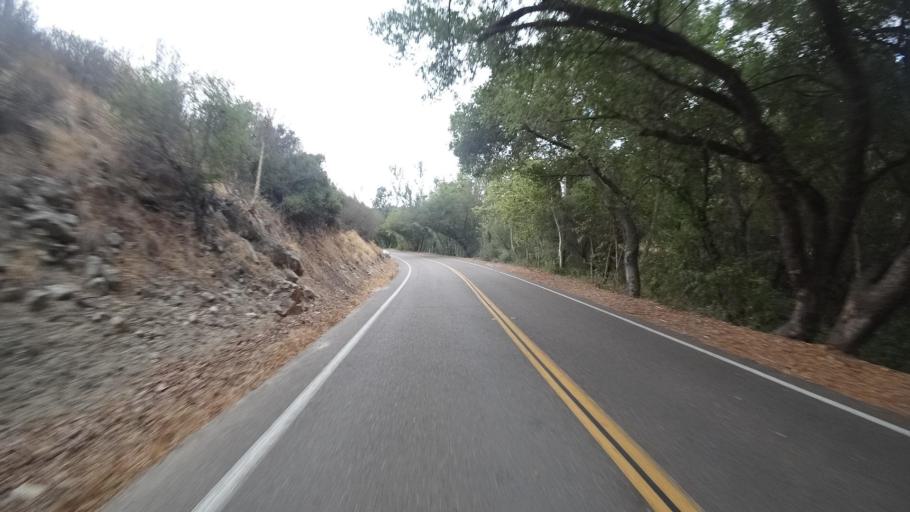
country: US
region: California
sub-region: San Diego County
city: Eucalyptus Hills
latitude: 32.9625
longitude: -116.9112
